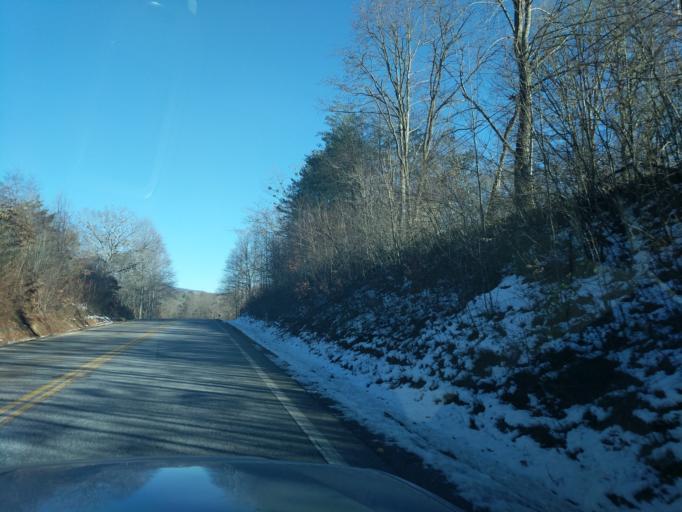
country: US
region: Georgia
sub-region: Towns County
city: Hiawassee
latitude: 34.9254
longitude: -83.6818
